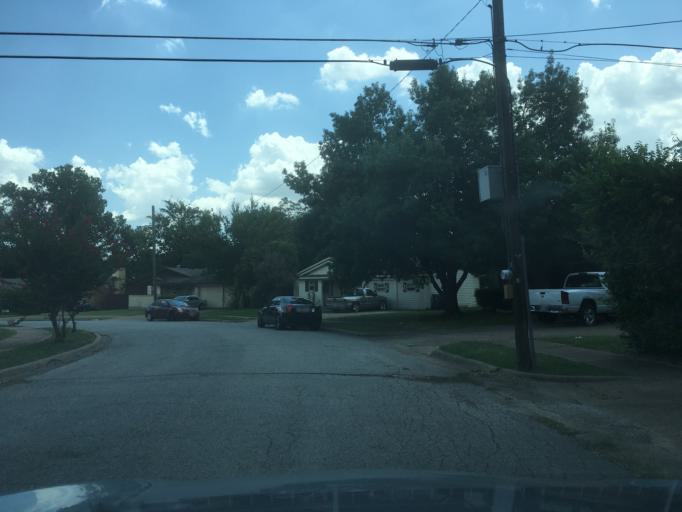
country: US
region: Texas
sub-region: Dallas County
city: Garland
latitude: 32.8734
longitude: -96.6473
